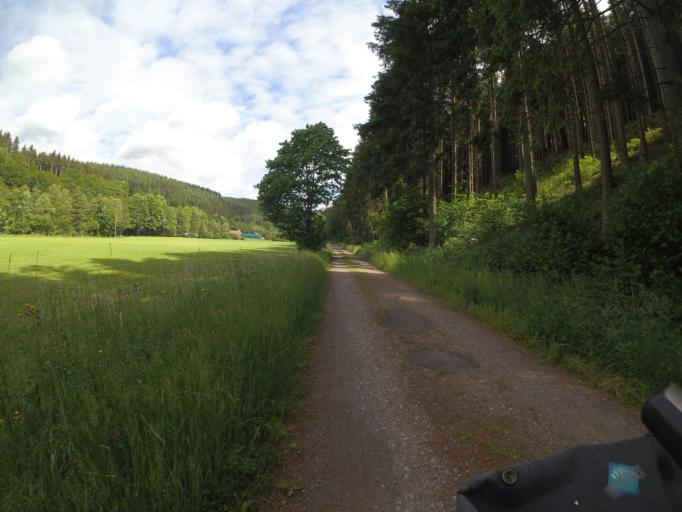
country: DE
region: North Rhine-Westphalia
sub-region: Regierungsbezirk Koln
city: Hellenthal
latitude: 50.4717
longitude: 6.4227
